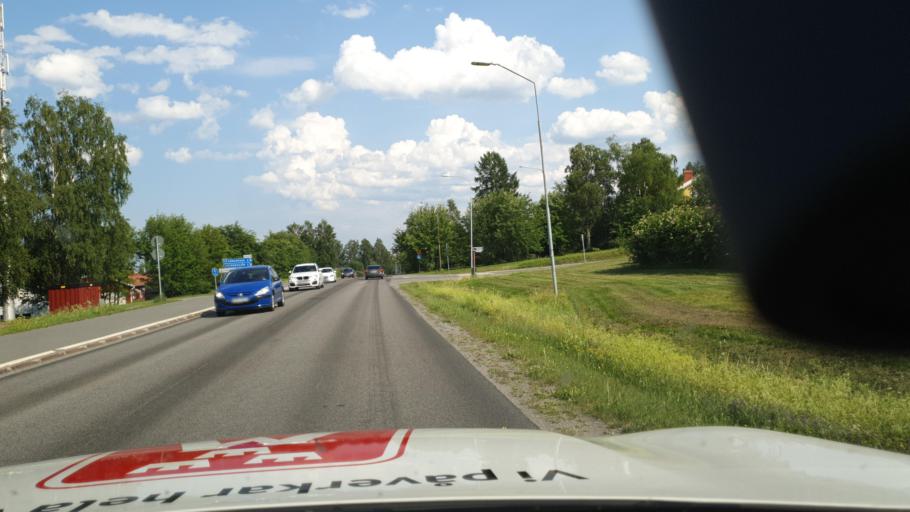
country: SE
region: Vaesterbotten
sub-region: Skelleftea Kommun
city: Viken
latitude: 64.7468
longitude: 20.9185
